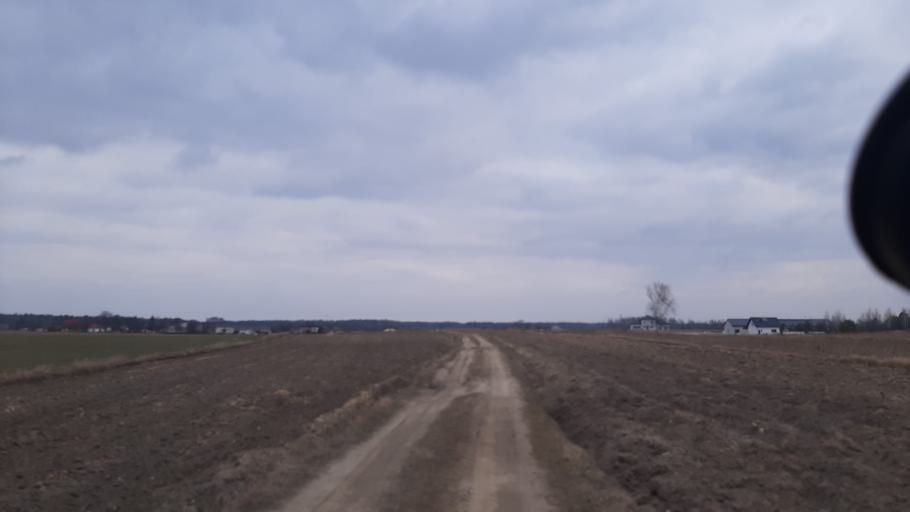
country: PL
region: Lublin Voivodeship
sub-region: Powiat lubelski
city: Garbow
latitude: 51.4052
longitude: 22.3910
